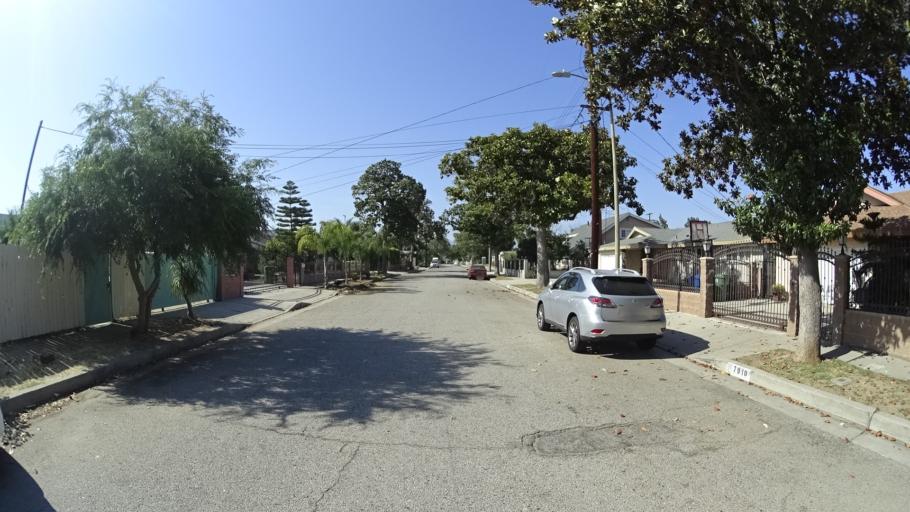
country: US
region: California
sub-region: Los Angeles County
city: Van Nuys
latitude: 34.2141
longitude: -118.4276
